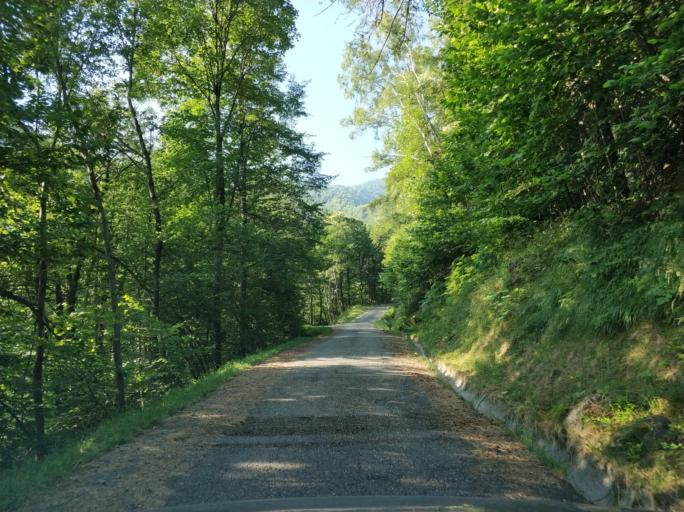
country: IT
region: Piedmont
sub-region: Provincia di Torino
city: Ceres
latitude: 45.3118
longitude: 7.3682
